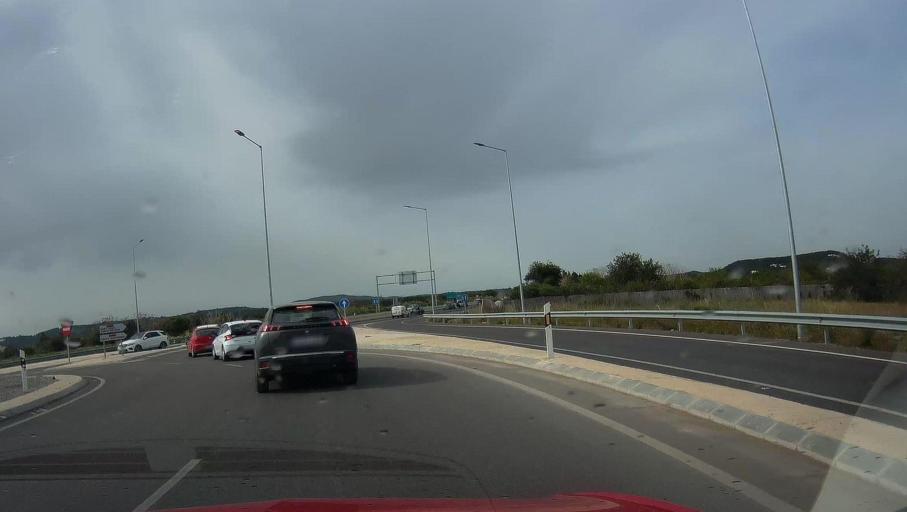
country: ES
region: Balearic Islands
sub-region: Illes Balears
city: Ibiza
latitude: 38.9360
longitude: 1.4445
